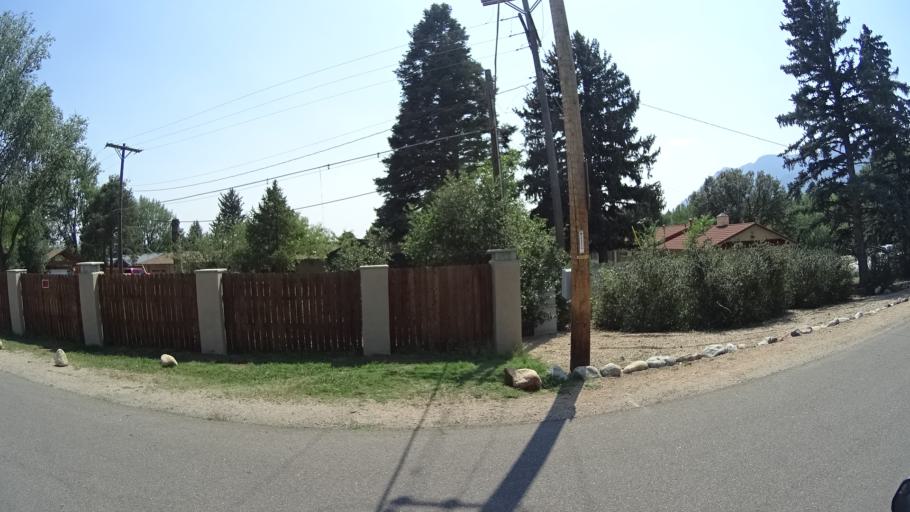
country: US
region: Colorado
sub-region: El Paso County
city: Colorado Springs
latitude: 38.7987
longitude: -104.8314
